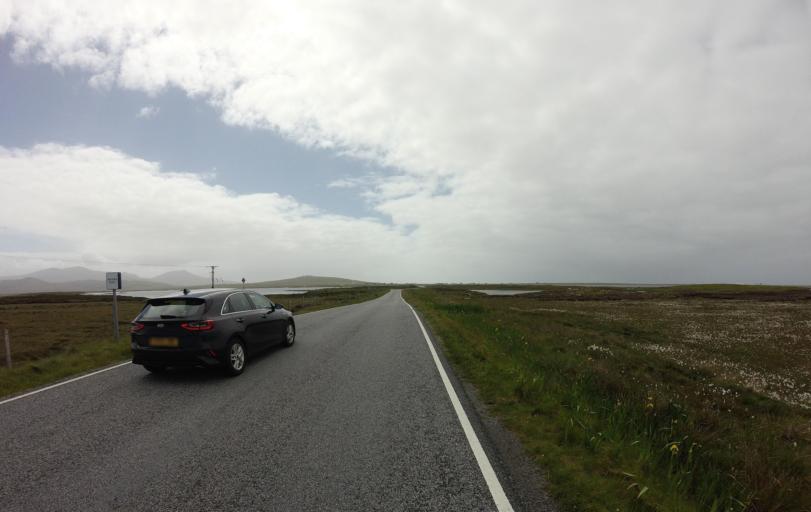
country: GB
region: Scotland
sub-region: Eilean Siar
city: Benbecula
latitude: 57.3673
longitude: -7.3513
